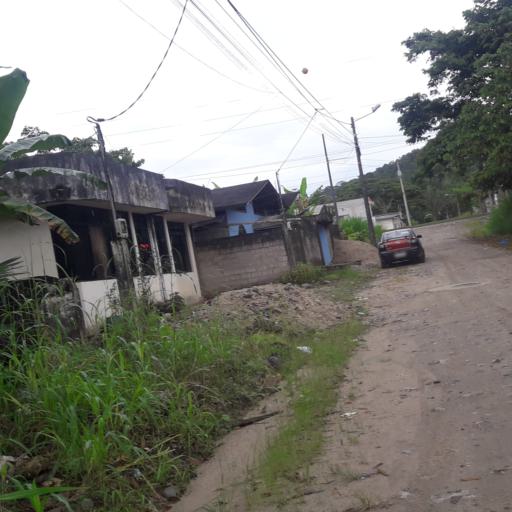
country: EC
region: Napo
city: Tena
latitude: -0.9886
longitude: -77.8083
